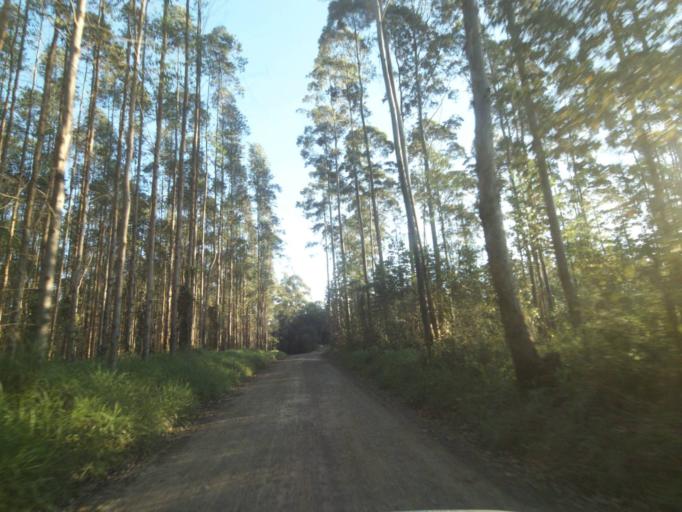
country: BR
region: Parana
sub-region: Telemaco Borba
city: Telemaco Borba
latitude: -24.4934
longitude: -50.5984
